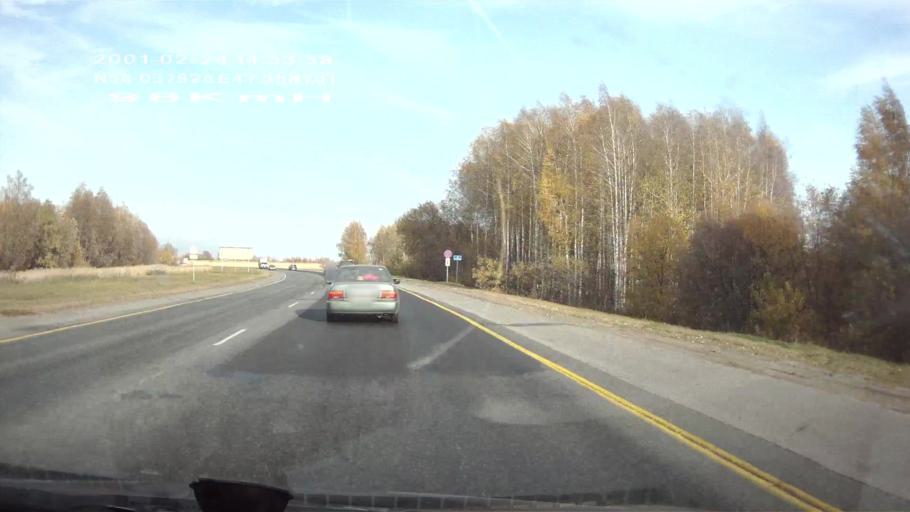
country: RU
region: Chuvashia
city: Kugesi
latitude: 56.0378
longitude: 47.3579
